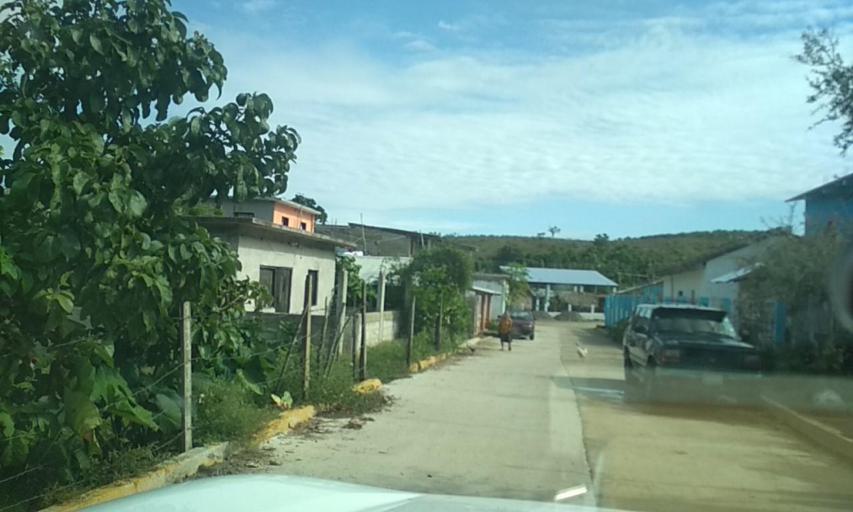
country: MX
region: Veracruz
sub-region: Papantla
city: Polutla
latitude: 20.5719
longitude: -97.1888
